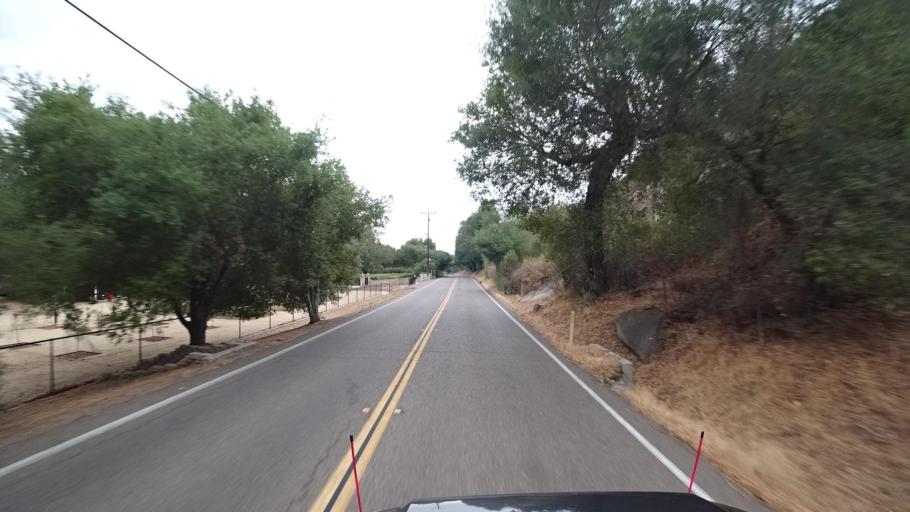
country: US
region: California
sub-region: San Diego County
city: Ramona
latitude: 32.9811
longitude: -116.9221
